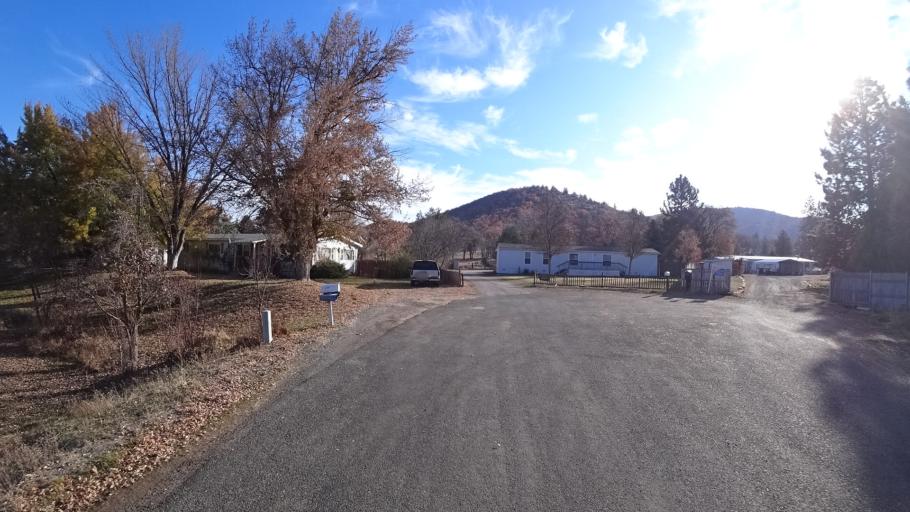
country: US
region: California
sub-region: Siskiyou County
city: Yreka
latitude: 41.6969
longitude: -122.6371
